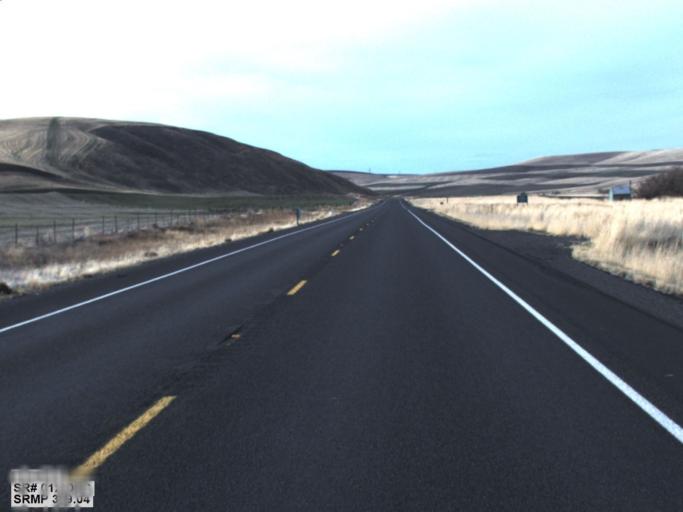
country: US
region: Washington
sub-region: Columbia County
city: Dayton
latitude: 46.5359
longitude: -117.8536
